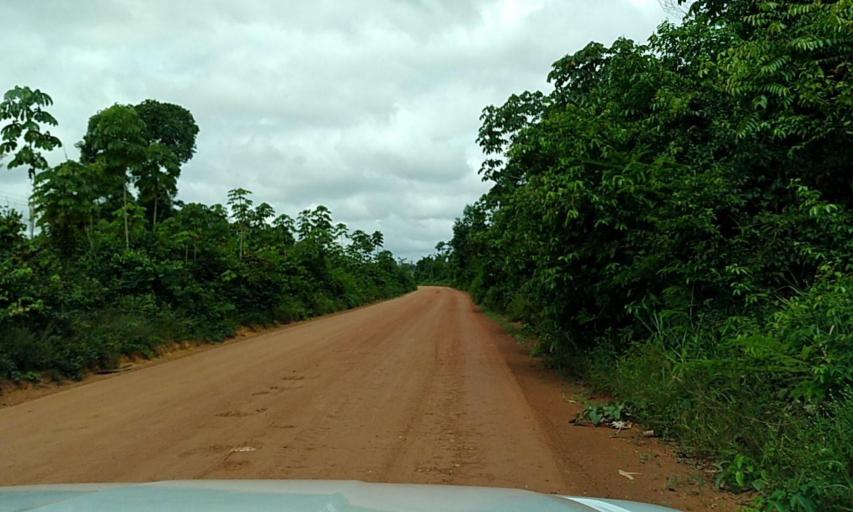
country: BR
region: Para
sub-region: Senador Jose Porfirio
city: Senador Jose Porfirio
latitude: -2.7917
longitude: -51.7624
